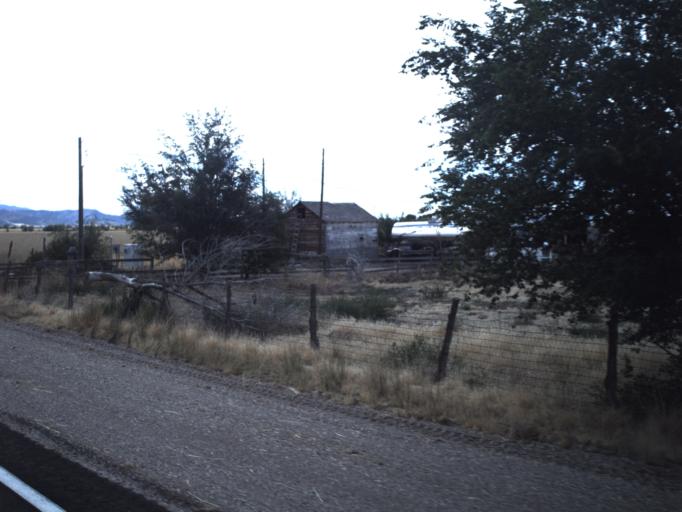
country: US
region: Utah
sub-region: Millard County
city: Fillmore
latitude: 38.8483
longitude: -112.4234
